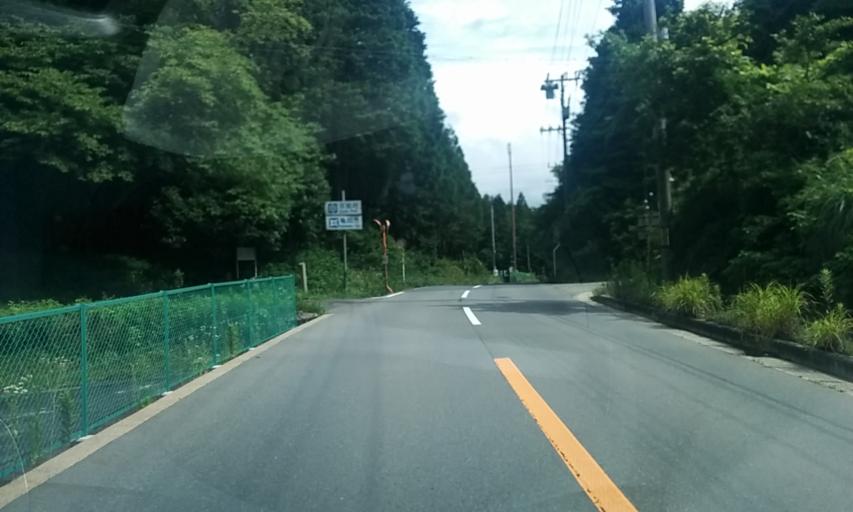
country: JP
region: Kyoto
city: Kameoka
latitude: 34.9937
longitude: 135.4765
